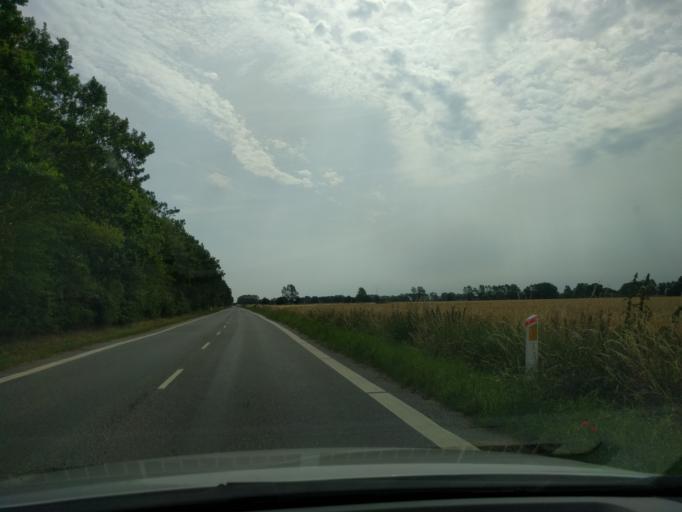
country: DK
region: South Denmark
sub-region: Nordfyns Kommune
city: Otterup
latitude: 55.5580
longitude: 10.4606
